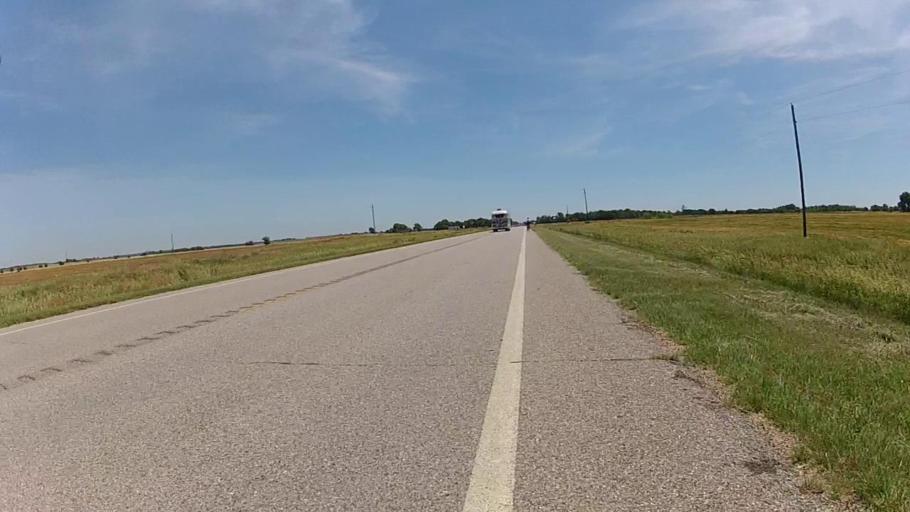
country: US
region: Kansas
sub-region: Barber County
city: Medicine Lodge
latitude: 37.2534
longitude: -98.4420
